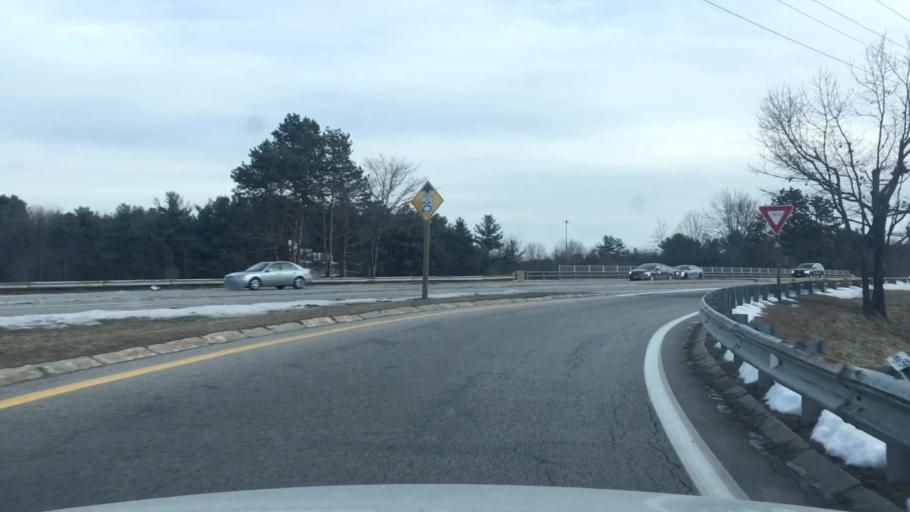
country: US
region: Maine
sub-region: York County
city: Kittery
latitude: 43.1053
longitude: -70.7483
